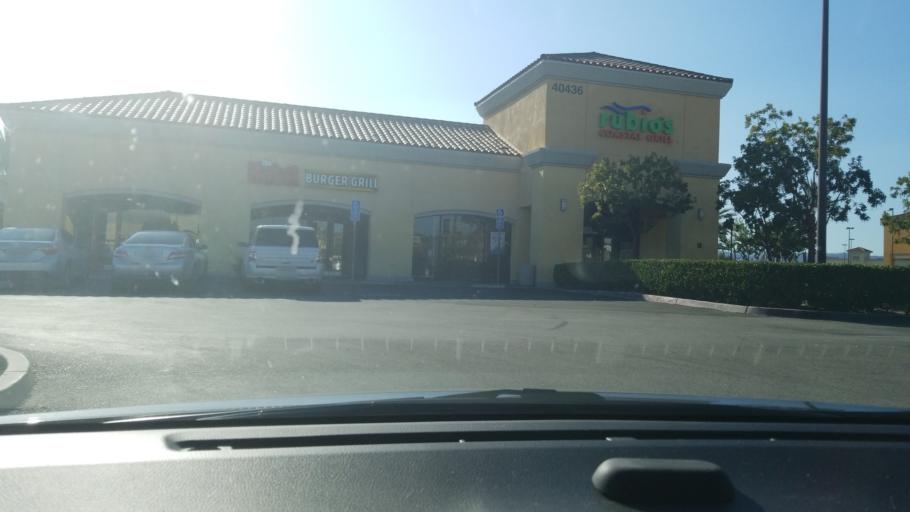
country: US
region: California
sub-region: Riverside County
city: Murrieta Hot Springs
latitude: 33.5550
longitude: -117.1767
